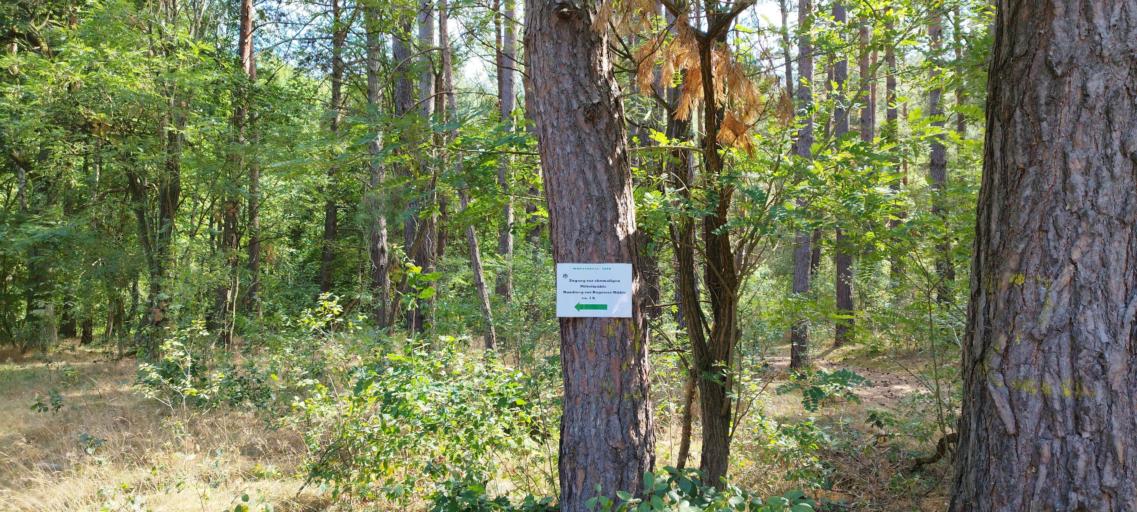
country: DE
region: Brandenburg
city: Mixdorf
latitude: 52.1952
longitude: 14.4313
